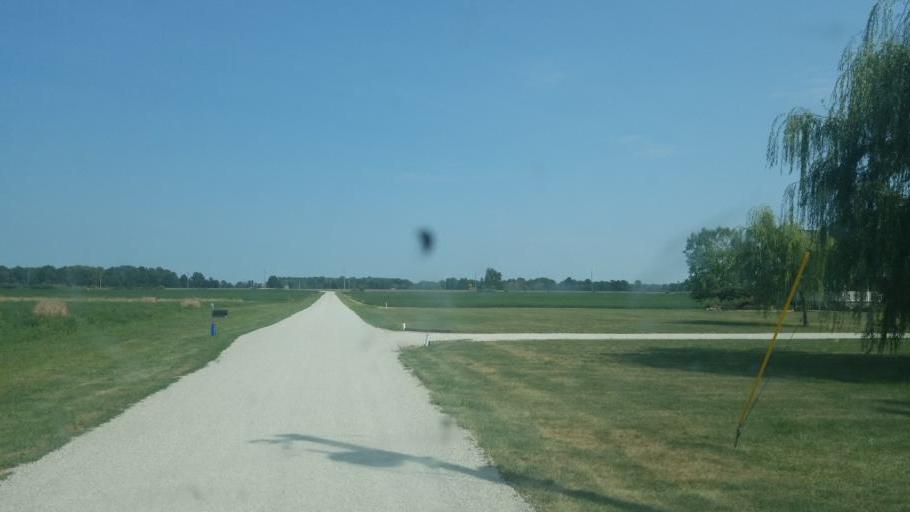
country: US
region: Ohio
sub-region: Crawford County
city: Crestline
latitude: 40.8251
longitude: -82.7123
